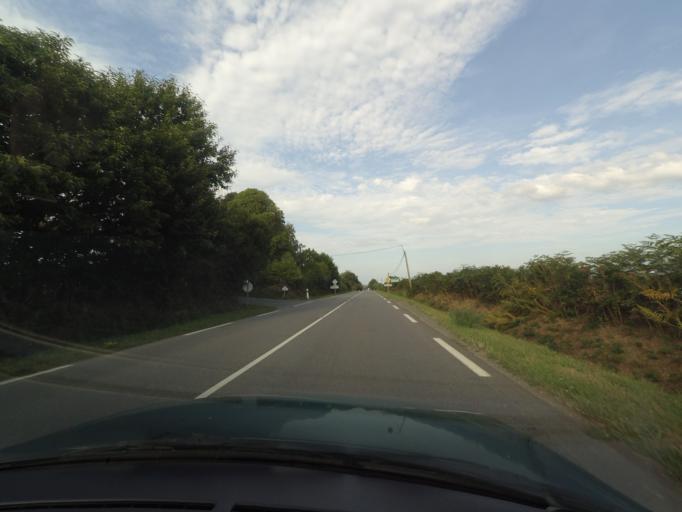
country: FR
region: Limousin
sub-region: Departement de la Haute-Vienne
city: Sereilhac
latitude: 45.7747
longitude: 1.0874
